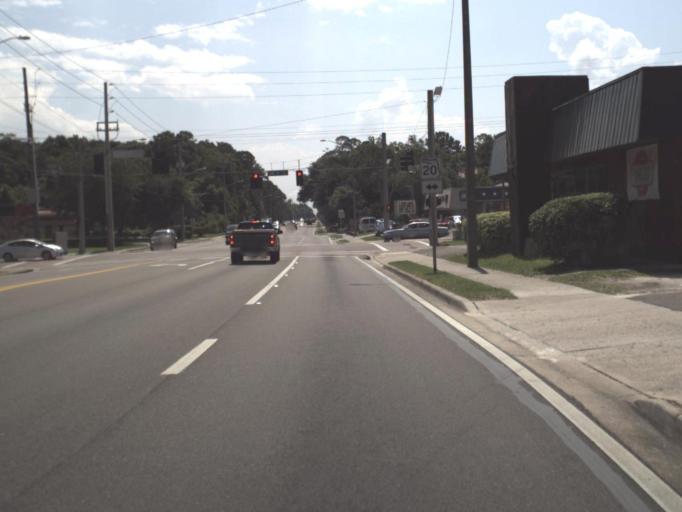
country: US
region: Florida
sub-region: Alachua County
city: Gainesville
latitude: 29.6739
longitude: -82.3315
